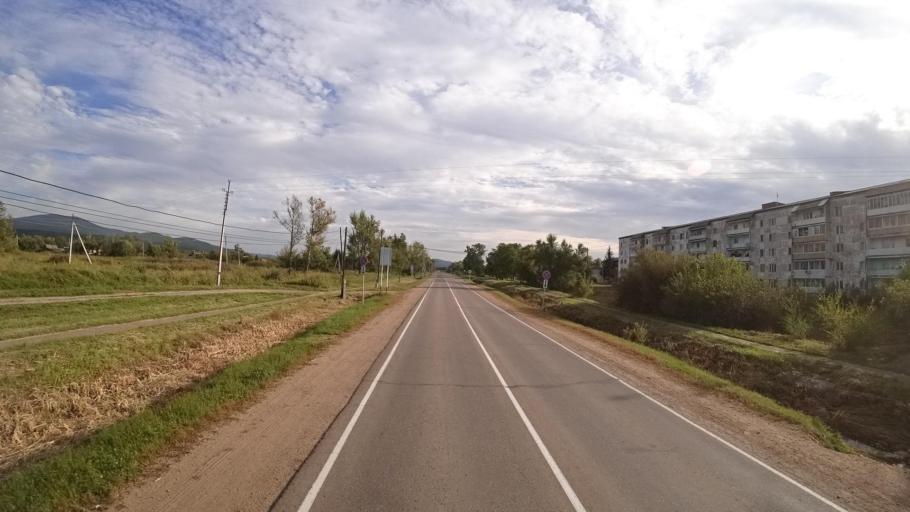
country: RU
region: Primorskiy
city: Dostoyevka
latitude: 44.2921
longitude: 133.4265
